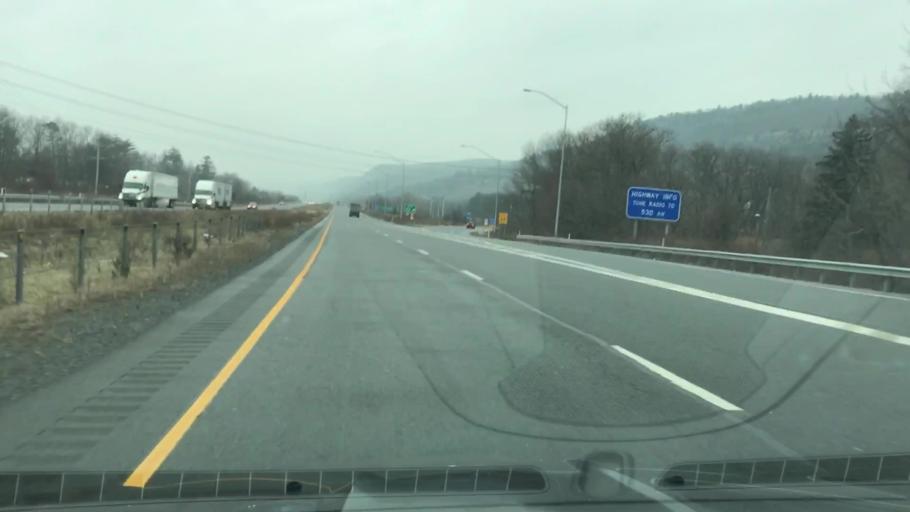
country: US
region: Pennsylvania
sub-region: Pike County
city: Matamoras
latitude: 41.3595
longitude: -74.7044
